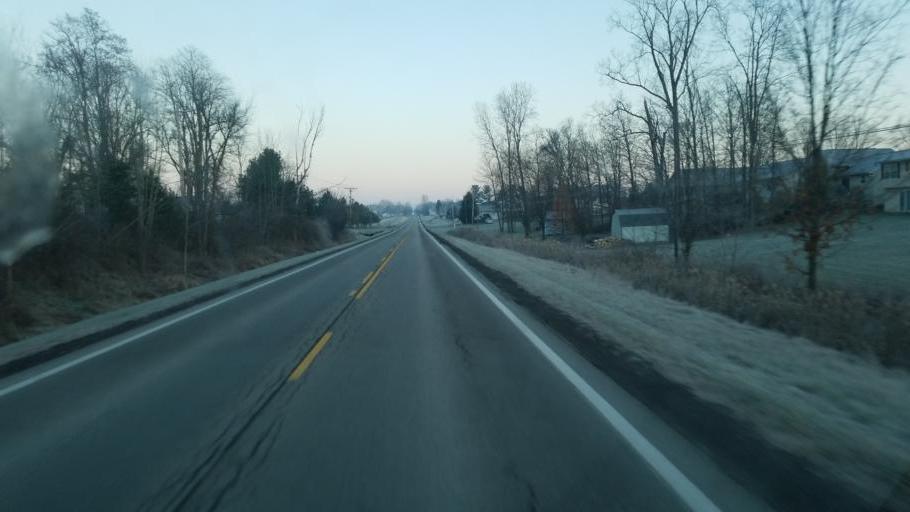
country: US
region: Ohio
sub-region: Wayne County
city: West Salem
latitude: 40.9595
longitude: -82.1095
